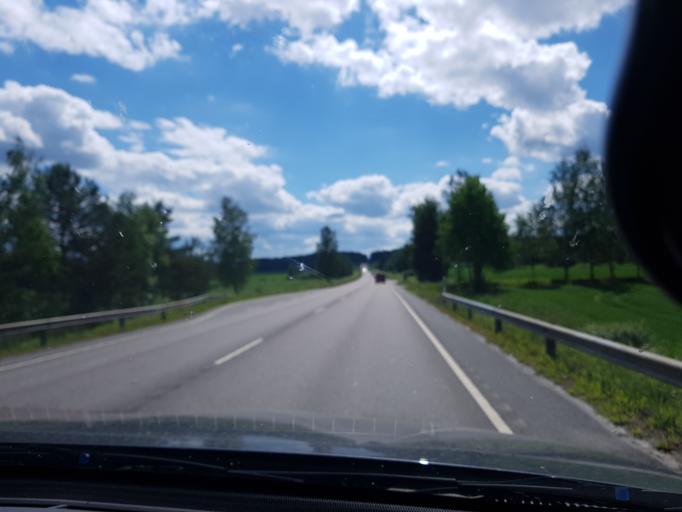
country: FI
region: Haeme
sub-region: Haemeenlinna
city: Parola
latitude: 61.1000
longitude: 24.4066
